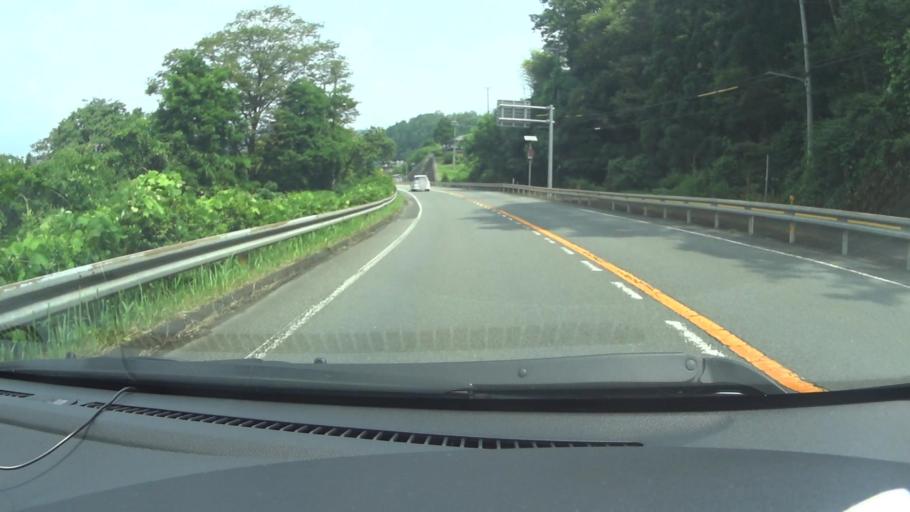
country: JP
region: Kyoto
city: Ayabe
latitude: 35.2844
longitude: 135.3358
